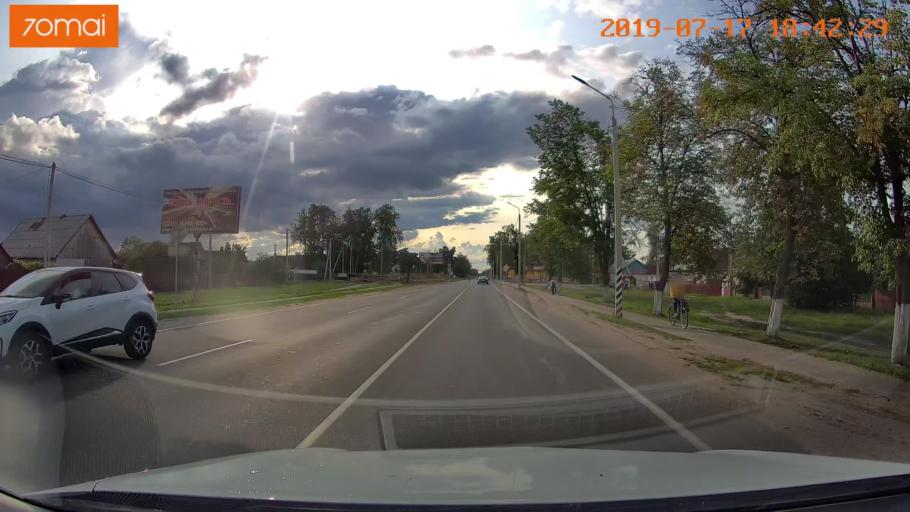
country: BY
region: Mogilev
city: Asipovichy
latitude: 53.3100
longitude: 28.6488
